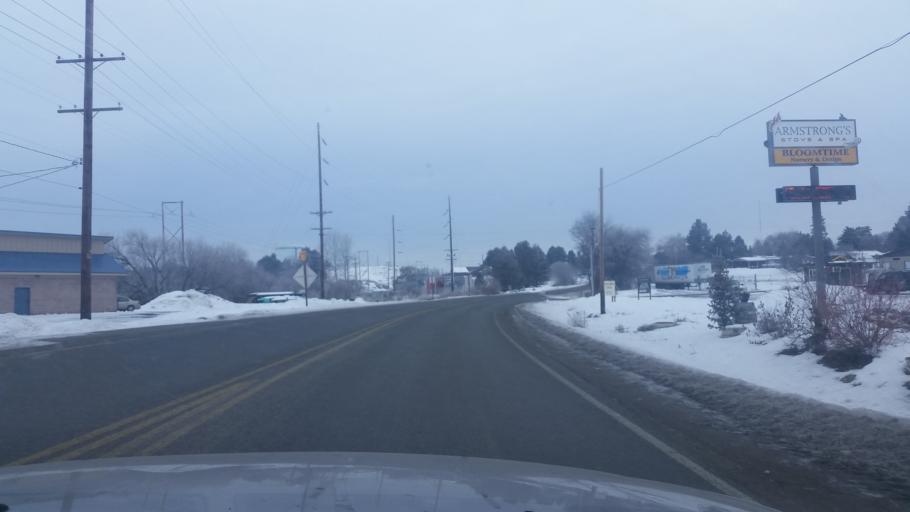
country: US
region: Washington
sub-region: Kittitas County
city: Ellensburg
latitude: 46.9997
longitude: -120.5197
